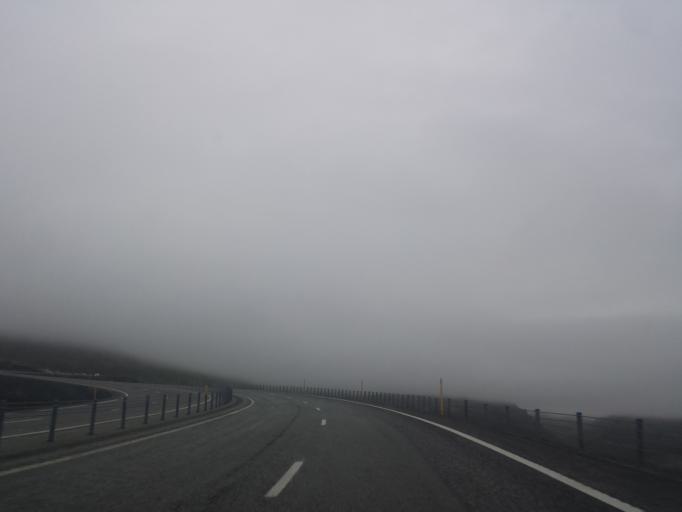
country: IS
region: South
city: Hveragerdi
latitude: 64.0127
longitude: -21.2219
